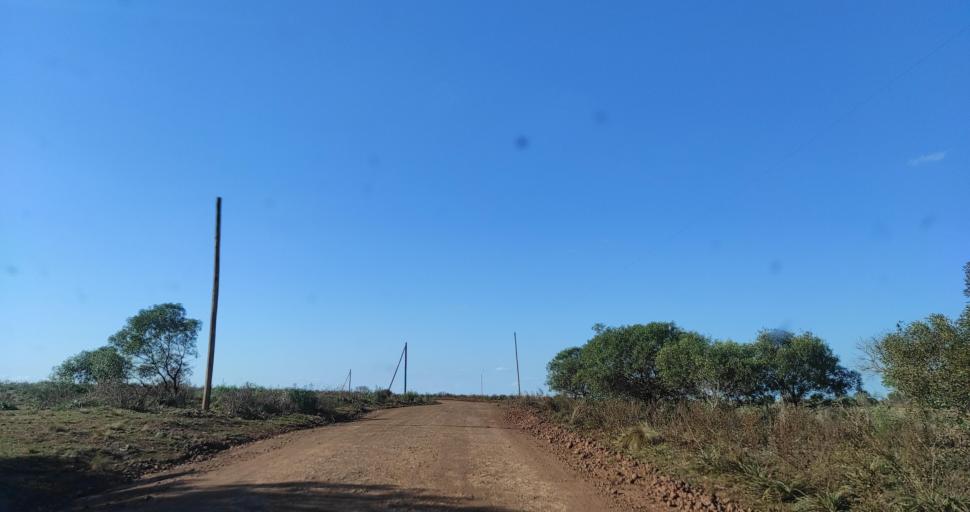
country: PY
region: Itapua
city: San Juan del Parana
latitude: -27.4443
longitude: -56.0621
